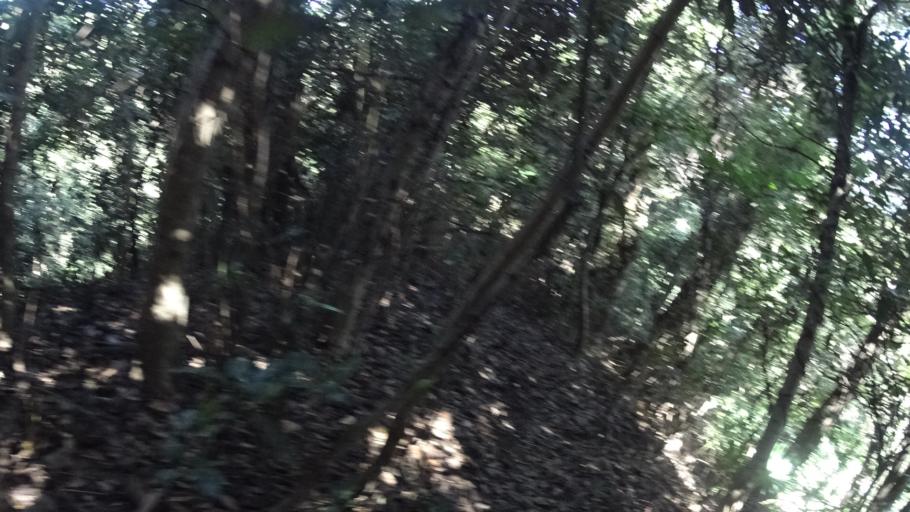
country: JP
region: Kanagawa
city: Hayama
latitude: 35.2729
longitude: 139.6014
